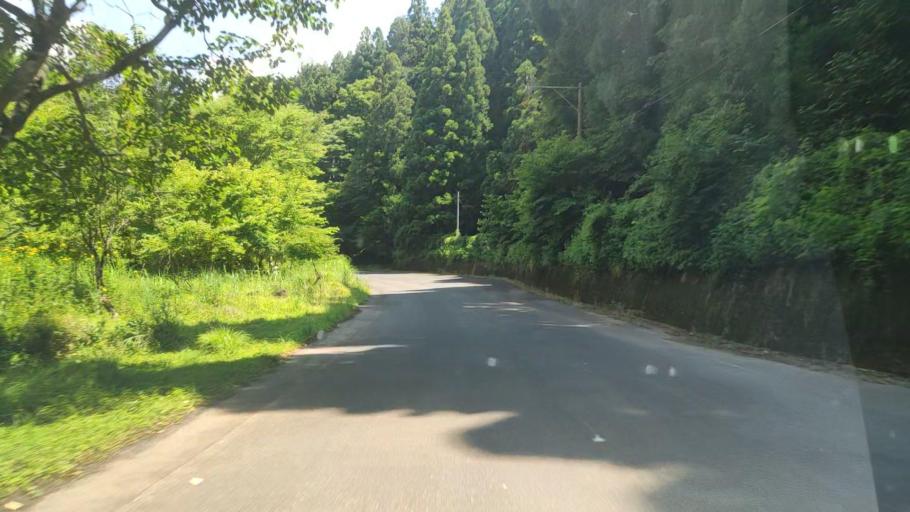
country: JP
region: Fukui
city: Ono
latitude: 35.7278
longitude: 136.5783
